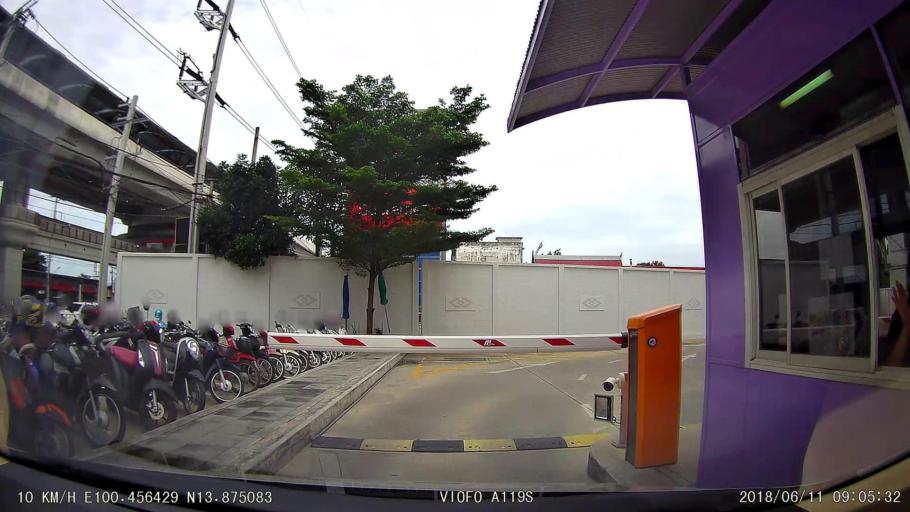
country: TH
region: Nonthaburi
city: Bang Bua Thong
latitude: 13.8759
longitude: 100.4570
